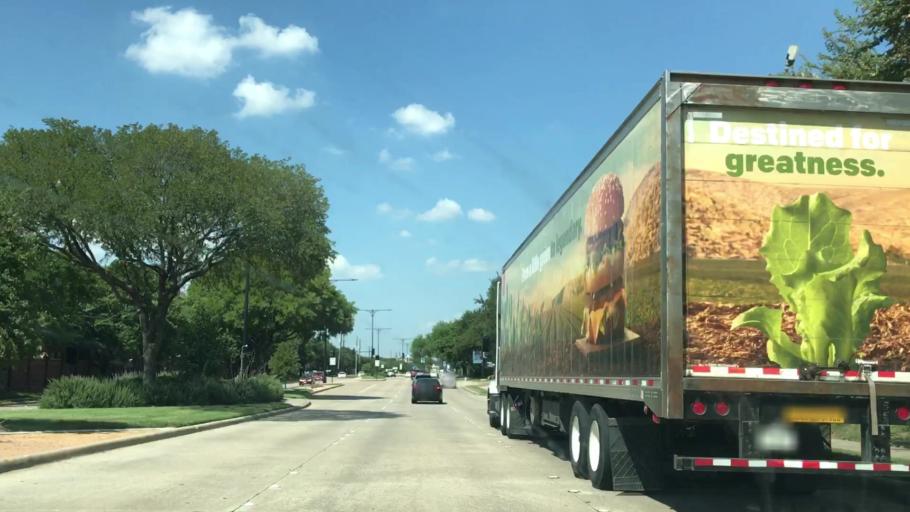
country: US
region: Texas
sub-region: Dallas County
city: Coppell
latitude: 32.9746
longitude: -96.9936
